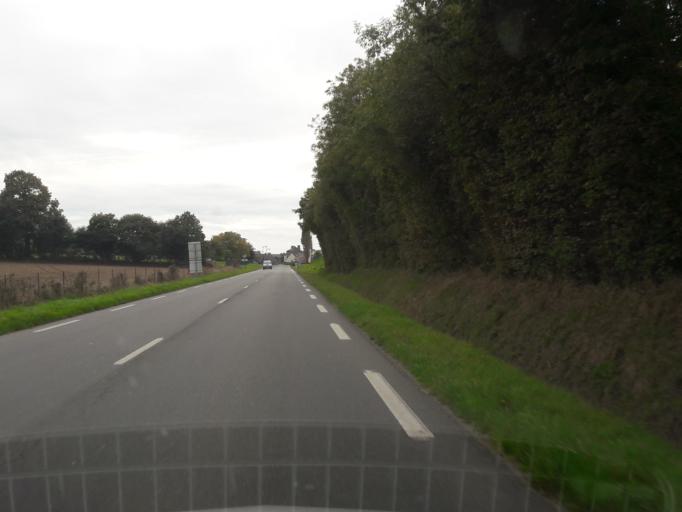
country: FR
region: Lower Normandy
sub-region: Departement du Calvados
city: Cahagnes
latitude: 49.0946
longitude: -0.7985
